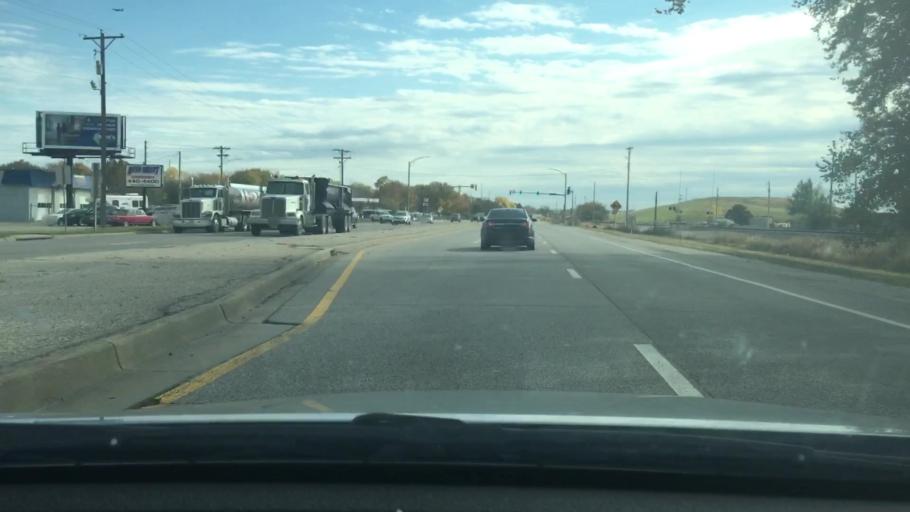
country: US
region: Kansas
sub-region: Sedgwick County
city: Wichita
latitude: 37.6359
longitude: -97.3043
